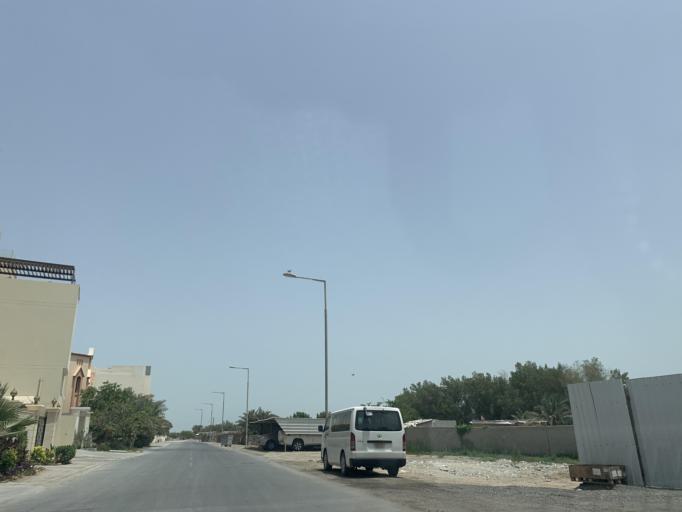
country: BH
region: Northern
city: Sitrah
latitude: 26.1532
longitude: 50.5854
